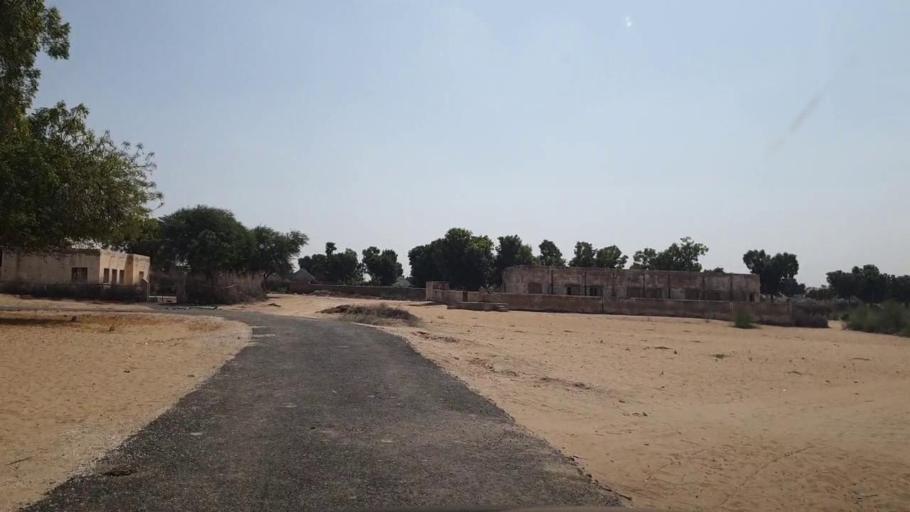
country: PK
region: Sindh
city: Islamkot
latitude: 25.0858
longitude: 70.6797
